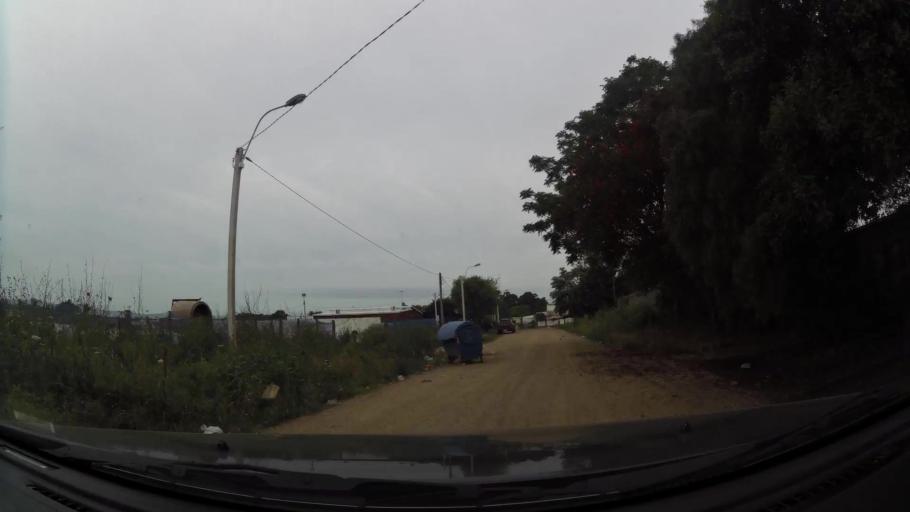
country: UY
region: Canelones
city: La Paz
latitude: -34.7489
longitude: -56.2157
